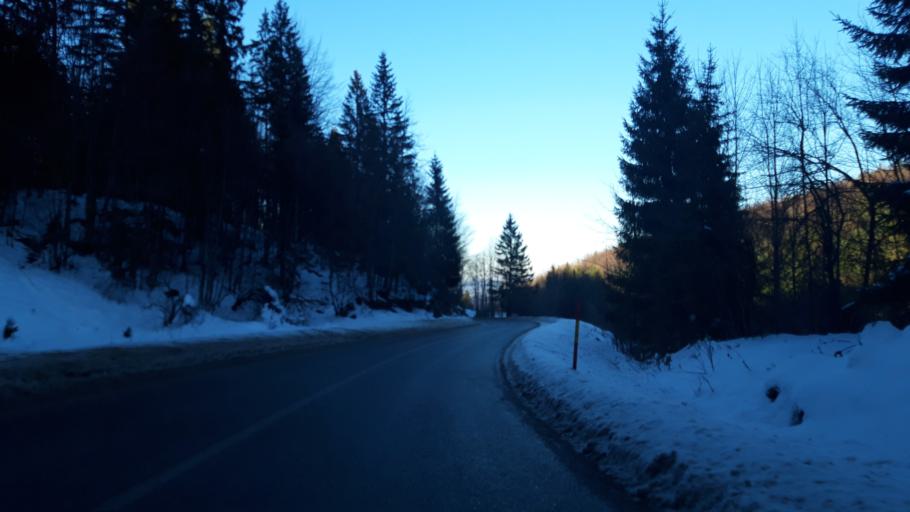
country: BA
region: Republika Srpska
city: Vlasenica
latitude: 44.1467
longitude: 18.9392
